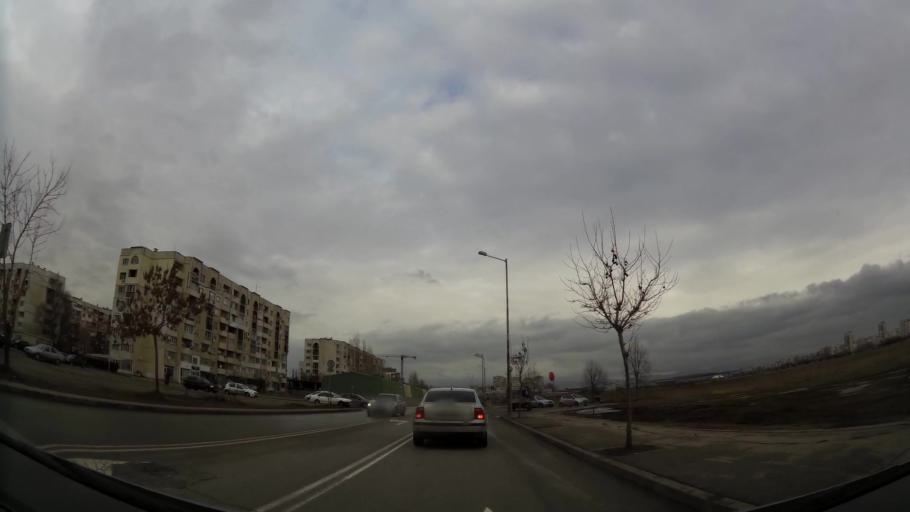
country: BG
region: Sofia-Capital
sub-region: Stolichna Obshtina
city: Sofia
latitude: 42.7368
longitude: 23.2726
